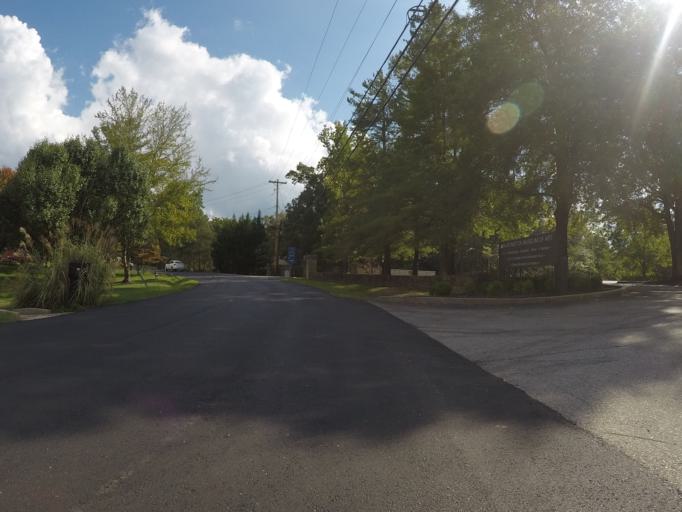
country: US
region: West Virginia
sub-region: Cabell County
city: Huntington
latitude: 38.3940
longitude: -82.4327
